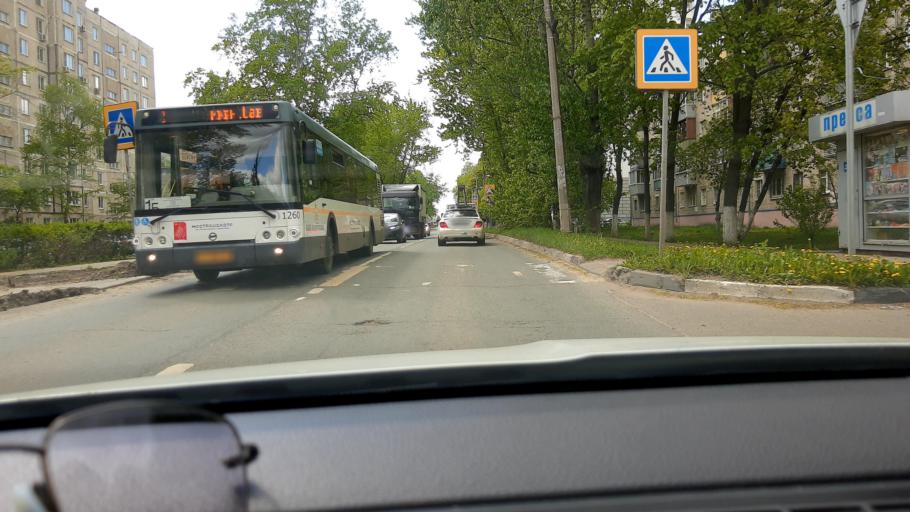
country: RU
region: Moskovskaya
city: Zheleznodorozhnyy
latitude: 55.7287
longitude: 38.0250
